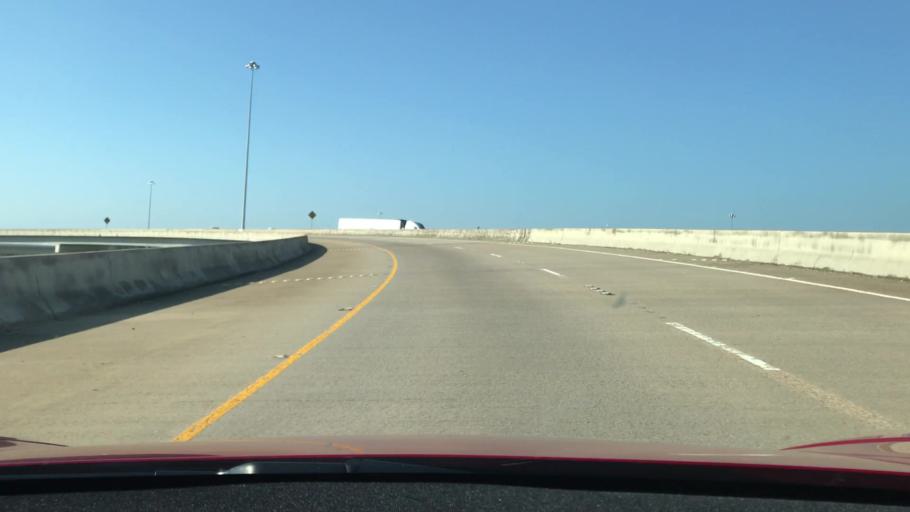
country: US
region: Louisiana
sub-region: Bossier Parish
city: Bossier City
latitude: 32.4205
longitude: -93.7501
